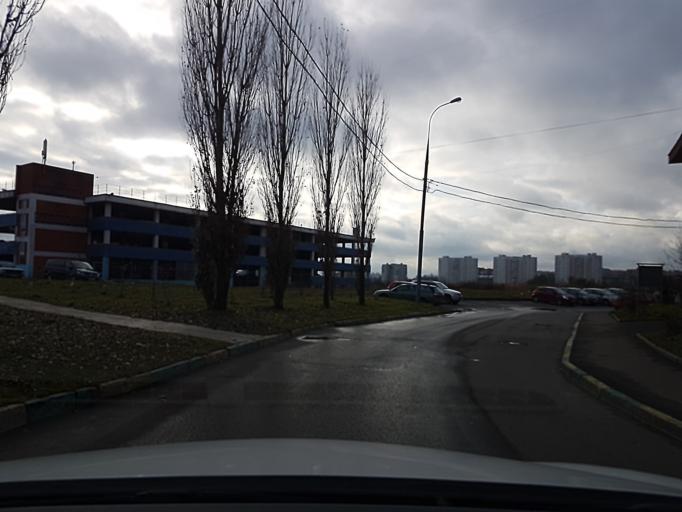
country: RU
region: Moskovskaya
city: Pavshino
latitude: 55.8269
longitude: 37.3512
